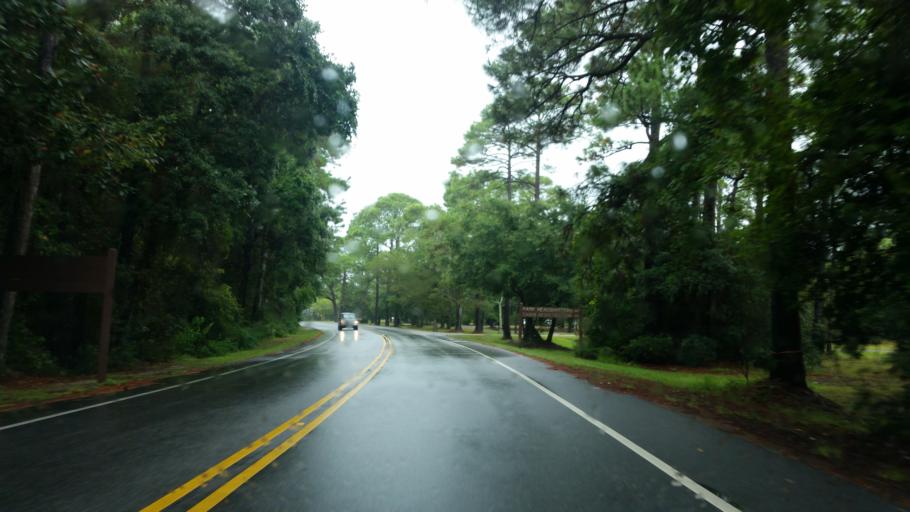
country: US
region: Alabama
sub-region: Baldwin County
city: Gulf Shores
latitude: 30.2664
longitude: -87.6796
